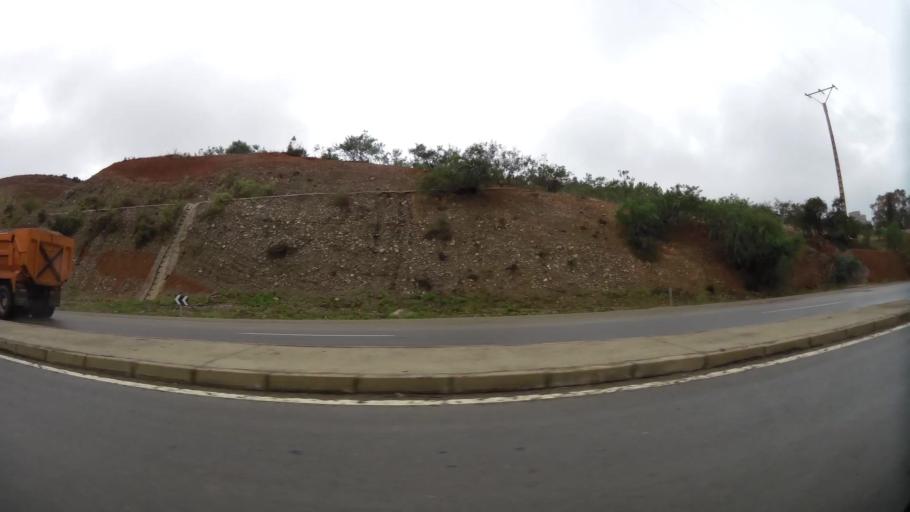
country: MA
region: Taza-Al Hoceima-Taounate
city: Imzourene
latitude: 35.1851
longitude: -3.8829
